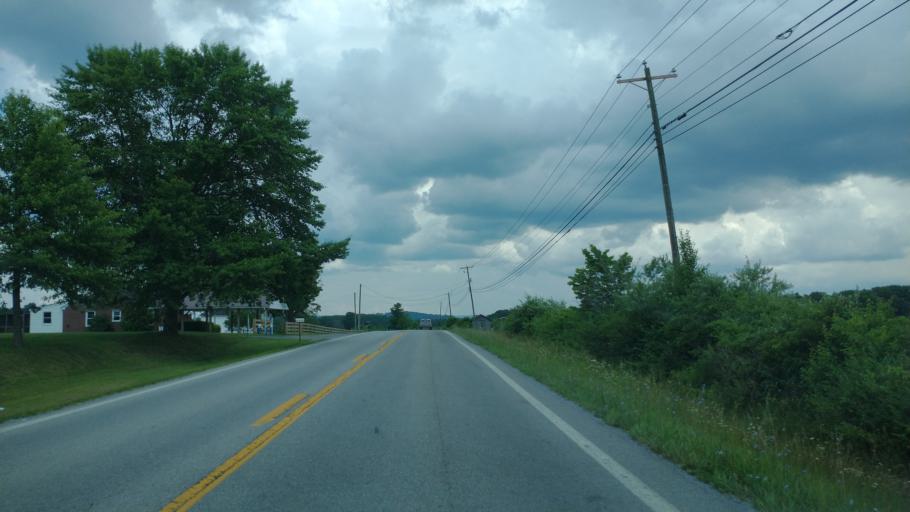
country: US
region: West Virginia
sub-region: Mercer County
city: Athens
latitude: 37.4524
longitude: -81.0080
